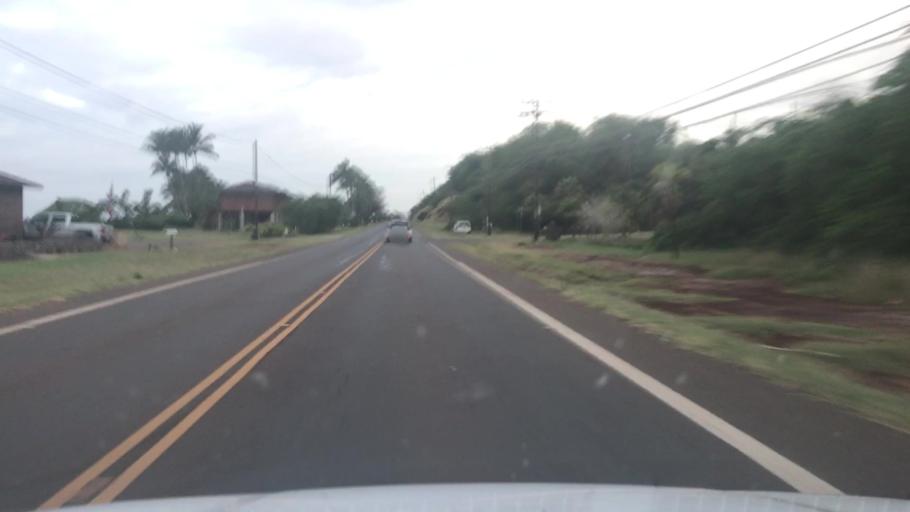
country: US
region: Hawaii
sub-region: Maui County
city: Kaunakakai
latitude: 21.0703
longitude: -156.9678
